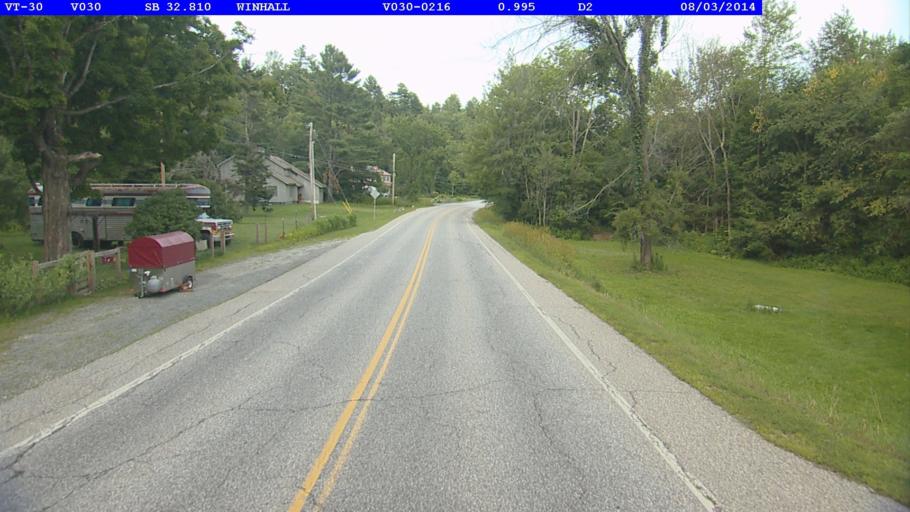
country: US
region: Vermont
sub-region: Bennington County
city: Manchester Center
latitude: 43.1444
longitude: -72.8858
